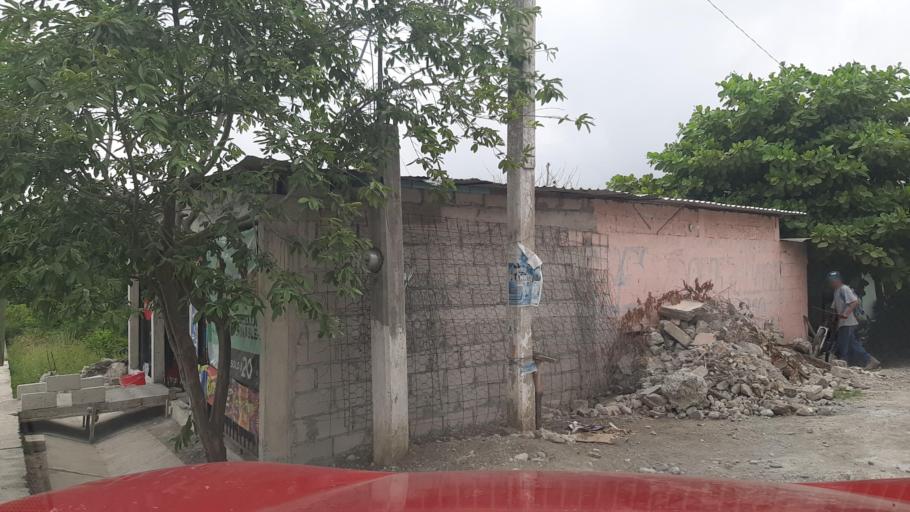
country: MX
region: Veracruz
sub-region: Papantla
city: Residencial Tajin
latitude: 20.6048
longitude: -97.4319
